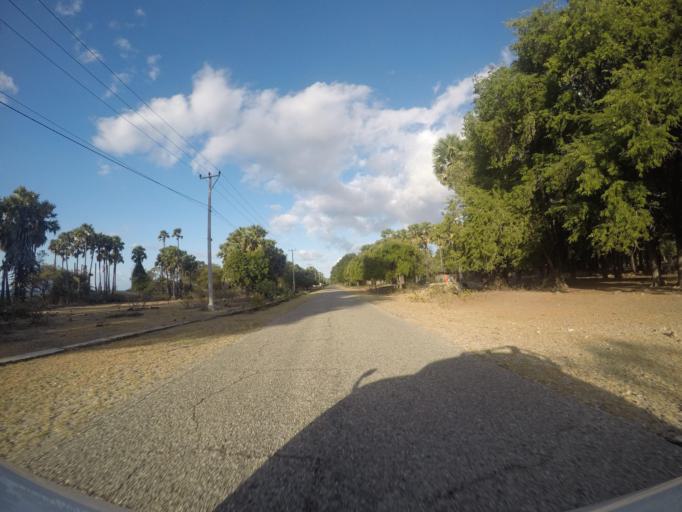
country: TL
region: Lautem
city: Lospalos
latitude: -8.3361
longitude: 126.9453
